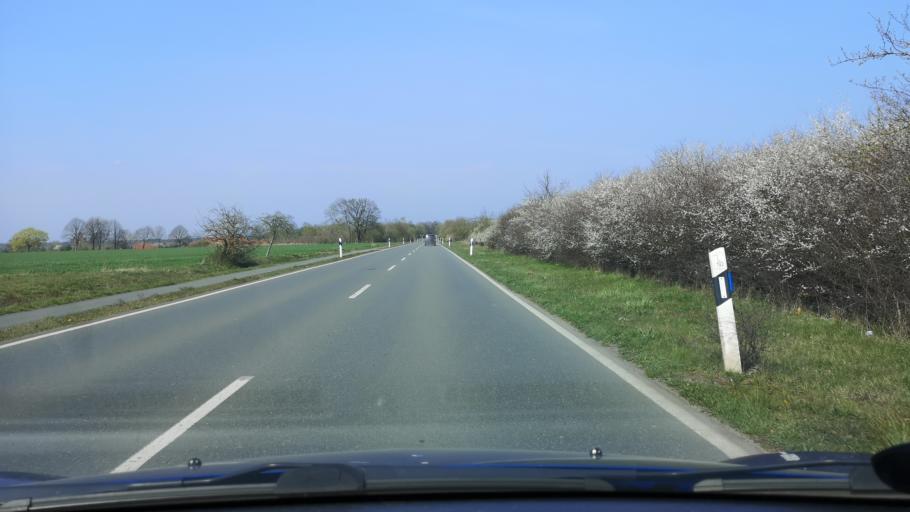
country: DE
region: Lower Saxony
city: Neustadt am Rubenberge
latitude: 52.5174
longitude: 9.4763
